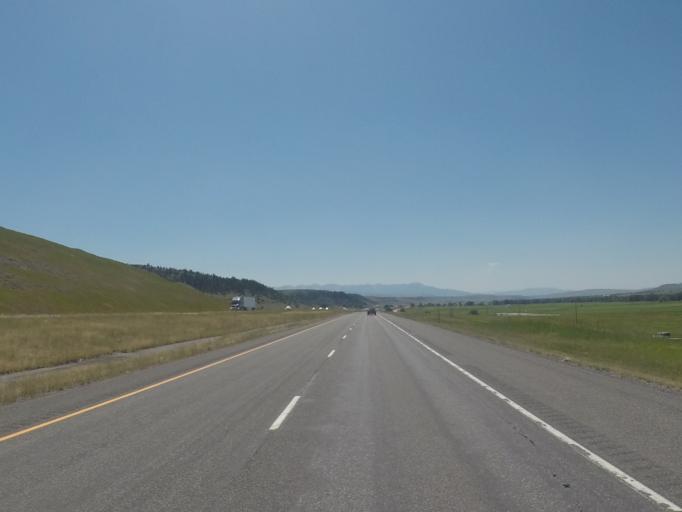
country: US
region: Montana
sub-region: Sweet Grass County
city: Big Timber
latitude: 45.7885
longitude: -110.0480
